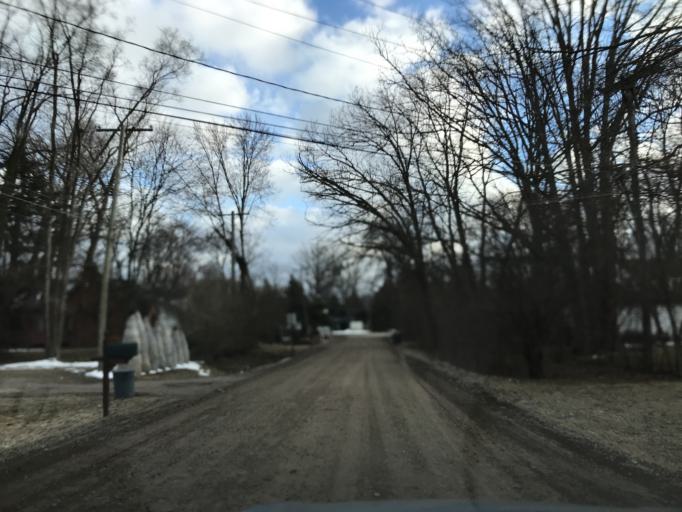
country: US
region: Michigan
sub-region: Oakland County
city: Farmington
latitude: 42.4535
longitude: -83.3272
